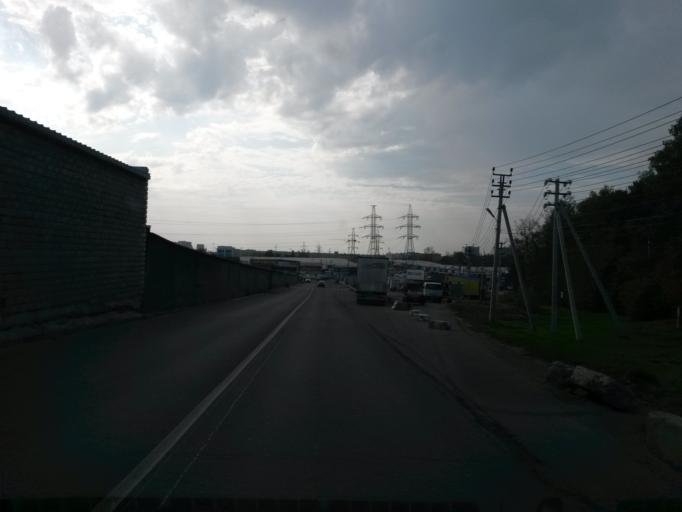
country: RU
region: Moscow
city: Tyoply Stan
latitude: 55.6074
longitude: 37.4836
